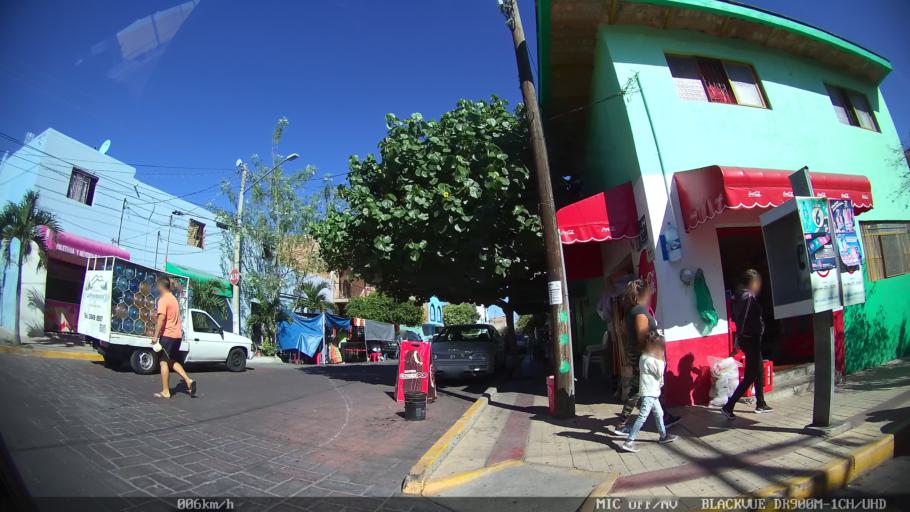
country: MX
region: Jalisco
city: Tlaquepaque
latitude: 20.6868
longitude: -103.2772
